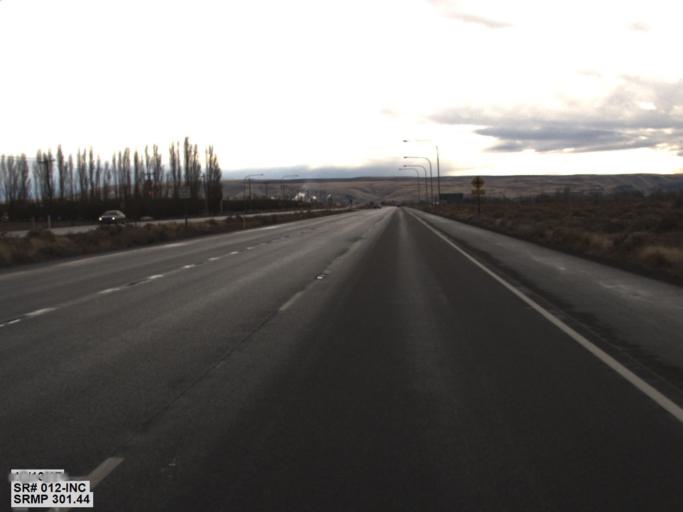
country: US
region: Washington
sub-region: Walla Walla County
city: Burbank
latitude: 46.1410
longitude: -118.9366
